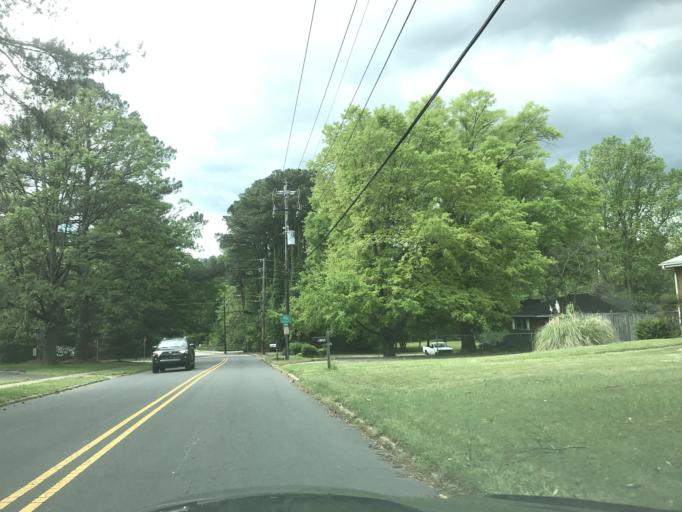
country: US
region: North Carolina
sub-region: Wake County
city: West Raleigh
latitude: 35.7755
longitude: -78.7097
